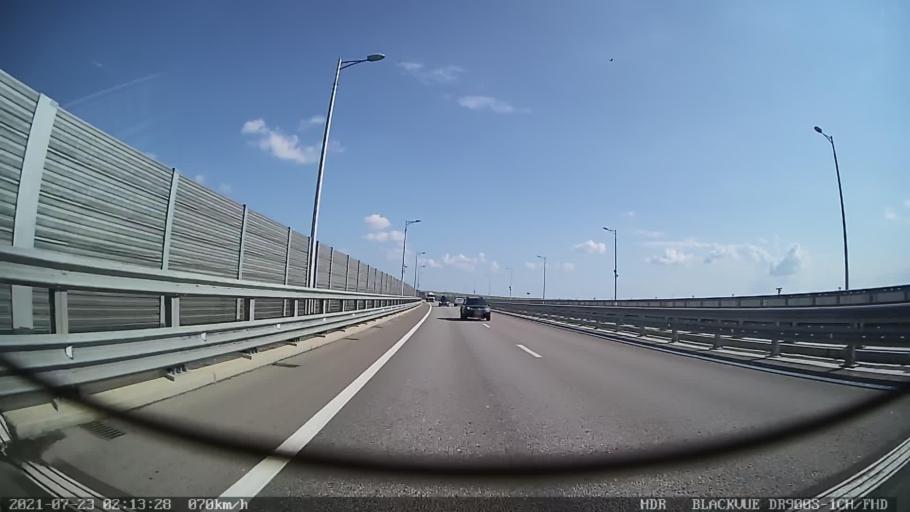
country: RU
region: Krasnodarskiy
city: Taman'
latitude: 45.2133
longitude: 36.6090
